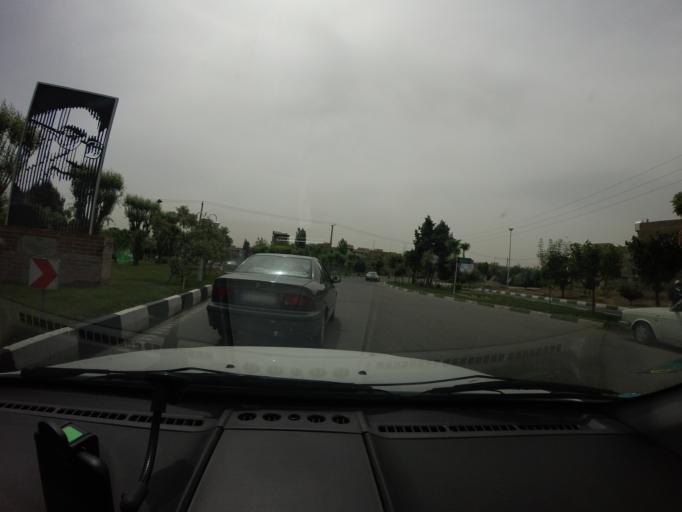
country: IR
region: Tehran
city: Eslamshahr
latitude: 35.5736
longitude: 51.2437
